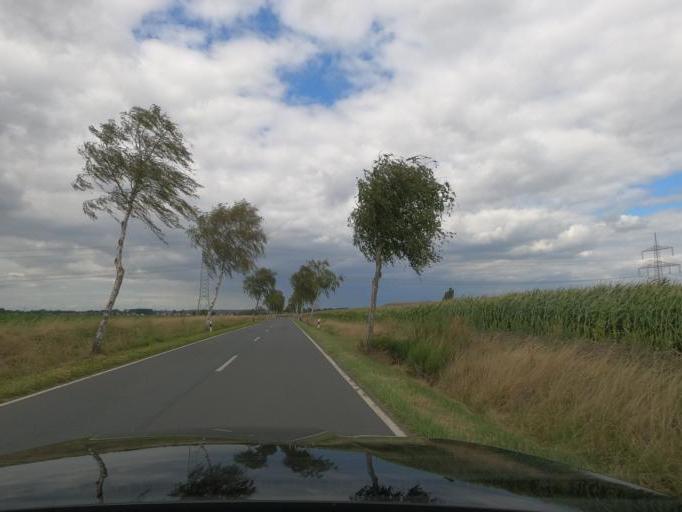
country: DE
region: Lower Saxony
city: Algermissen
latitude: 52.2812
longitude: 9.9502
